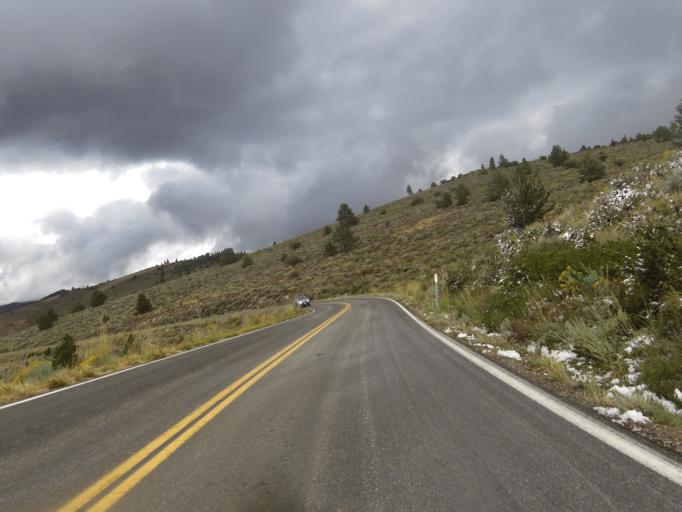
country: US
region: Nevada
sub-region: Douglas County
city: Gardnerville Ranchos
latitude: 38.6683
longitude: -119.6491
